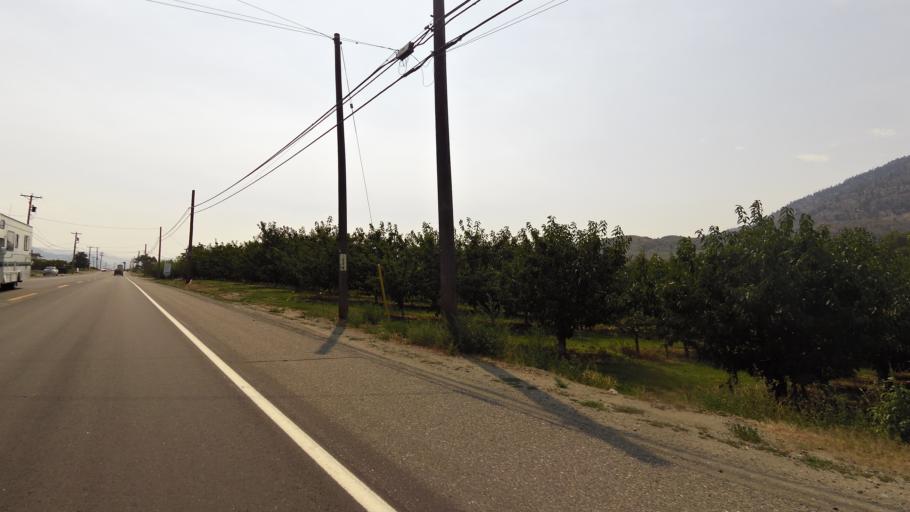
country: CA
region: British Columbia
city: Osoyoos
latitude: 49.0455
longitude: -119.4939
